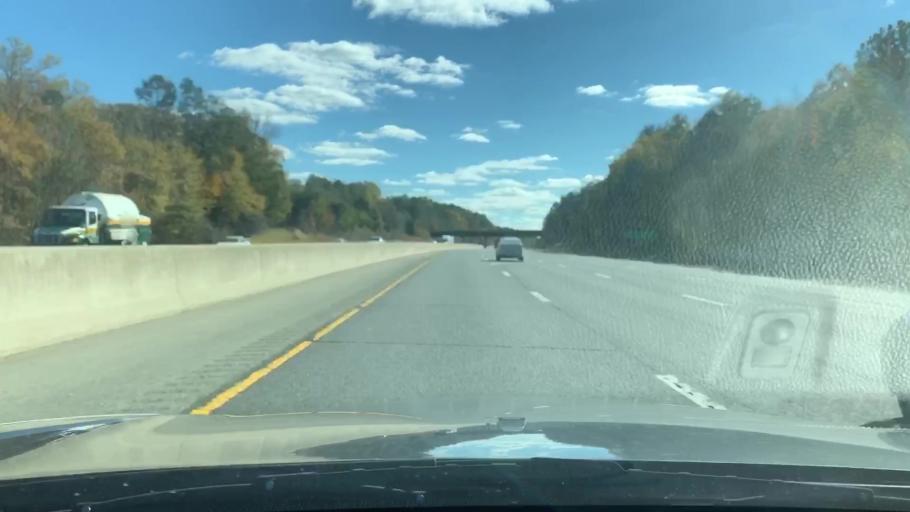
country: US
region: North Carolina
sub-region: Orange County
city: Chapel Hill
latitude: 35.9478
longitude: -78.9963
